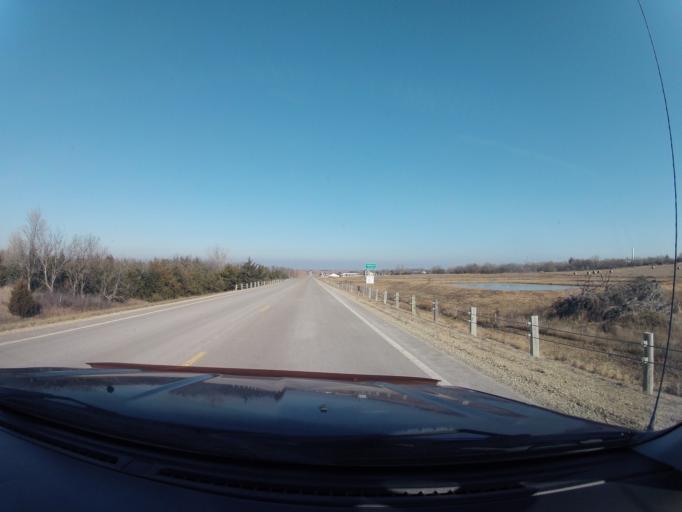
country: US
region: Kansas
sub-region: Marshall County
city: Blue Rapids
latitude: 39.4250
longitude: -96.7644
